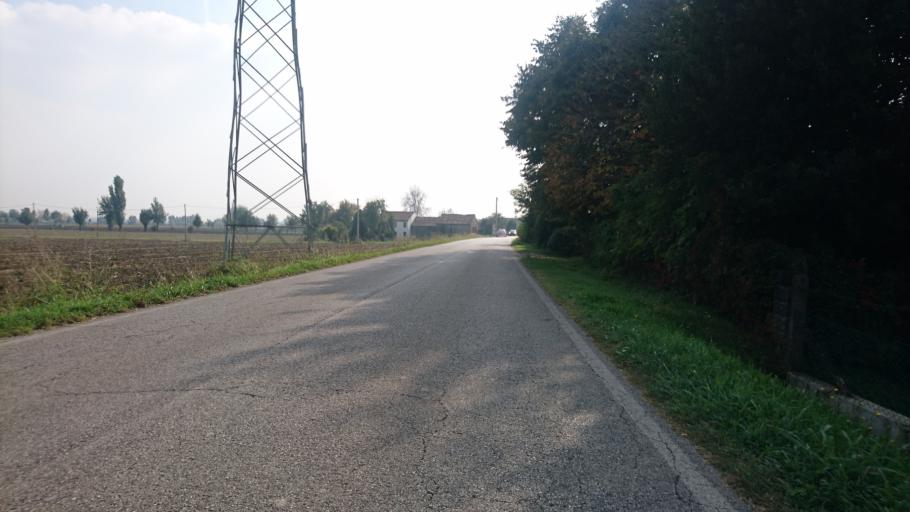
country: IT
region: Veneto
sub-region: Provincia di Rovigo
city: Grignano Polesine
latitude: 45.0313
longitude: 11.7505
